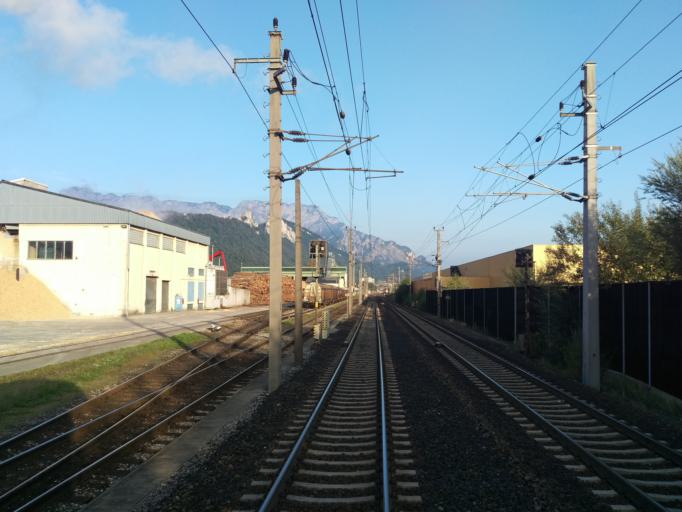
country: AT
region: Salzburg
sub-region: Politischer Bezirk Hallein
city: Hallein
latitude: 47.6775
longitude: 13.1119
